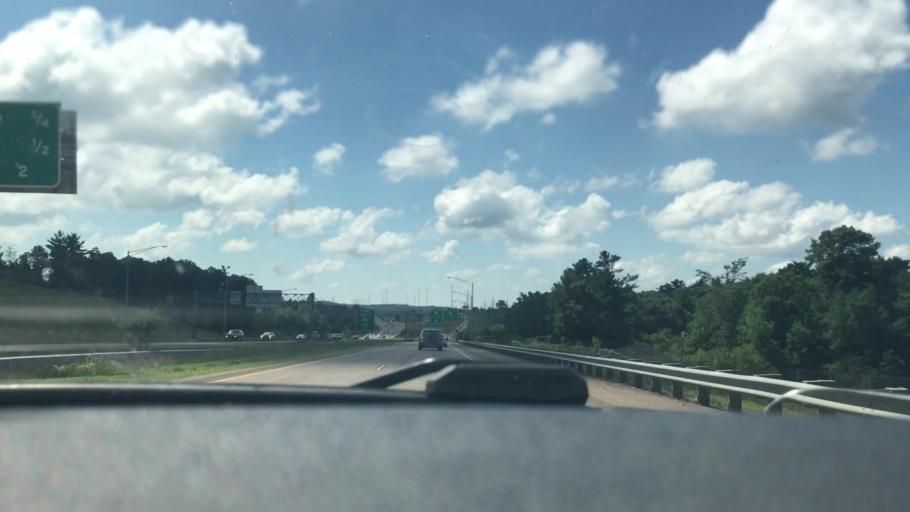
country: US
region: Wisconsin
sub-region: Eau Claire County
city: Altoona
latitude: 44.8045
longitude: -91.4558
